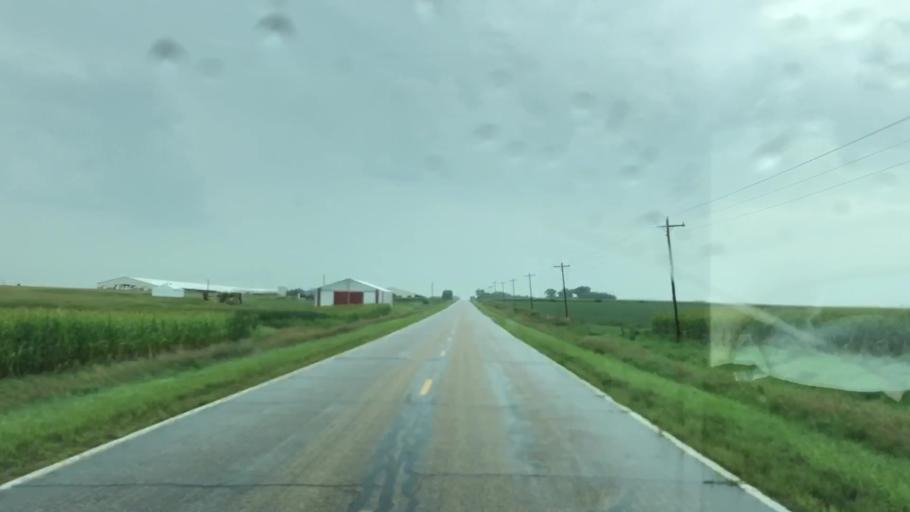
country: US
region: Iowa
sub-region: O'Brien County
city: Sanborn
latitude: 43.2728
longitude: -95.6882
